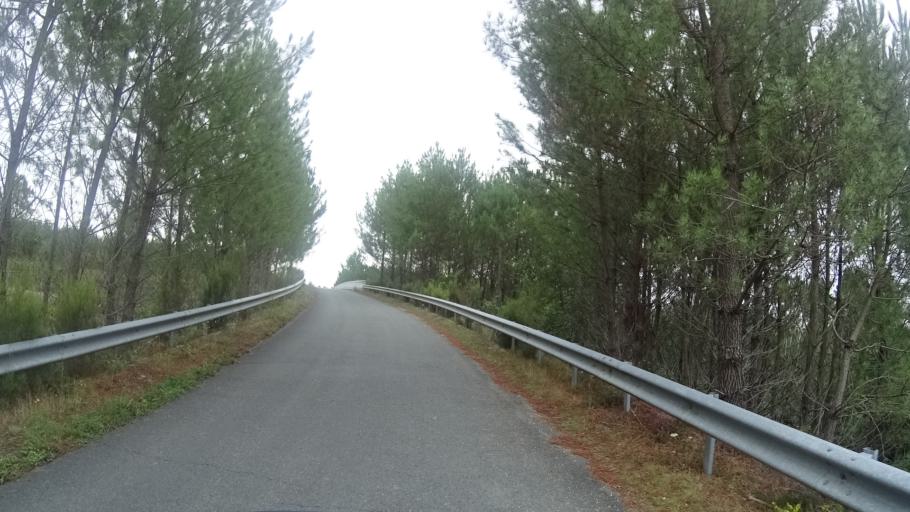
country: FR
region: Aquitaine
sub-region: Departement de la Dordogne
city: Sourzac
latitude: 45.0331
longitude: 0.3999
